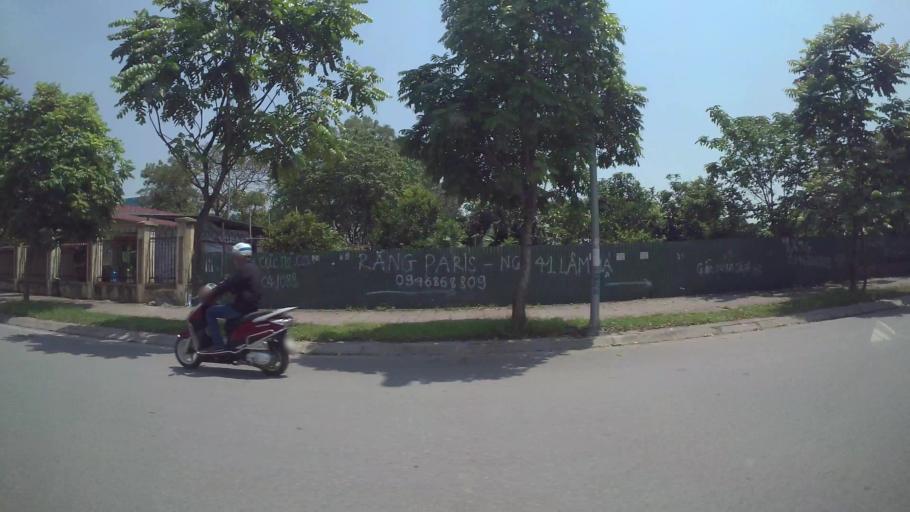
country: VN
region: Ha Noi
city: Hoan Kiem
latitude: 21.0419
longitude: 105.8821
